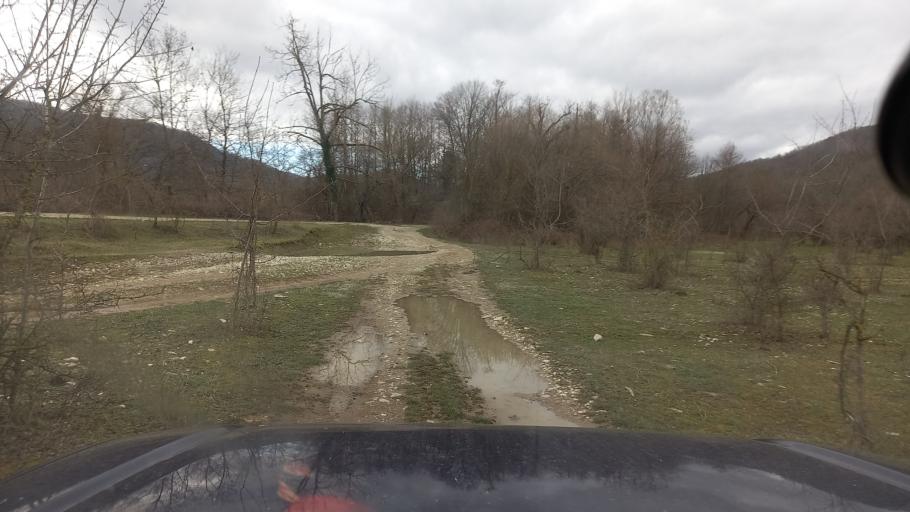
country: RU
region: Krasnodarskiy
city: Pshada
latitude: 44.4854
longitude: 38.4064
